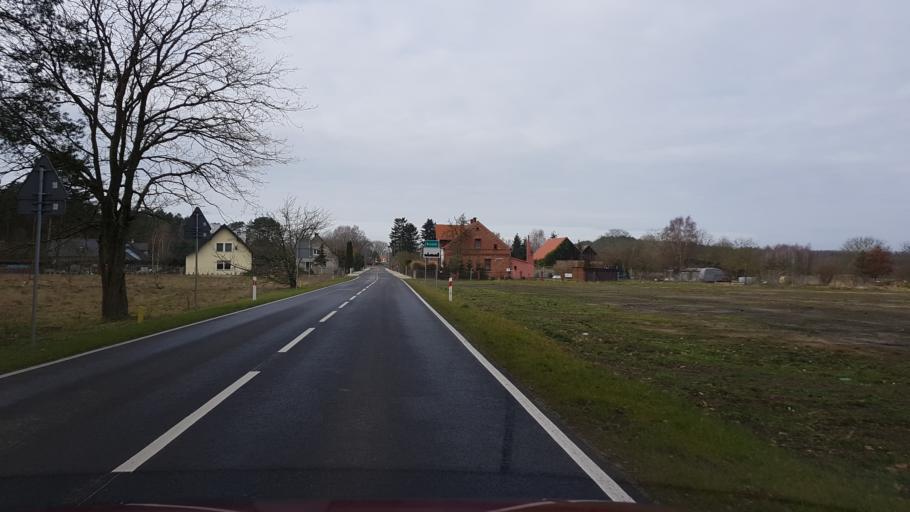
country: PL
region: West Pomeranian Voivodeship
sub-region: Powiat policki
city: Nowe Warpno
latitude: 53.6719
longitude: 14.3980
